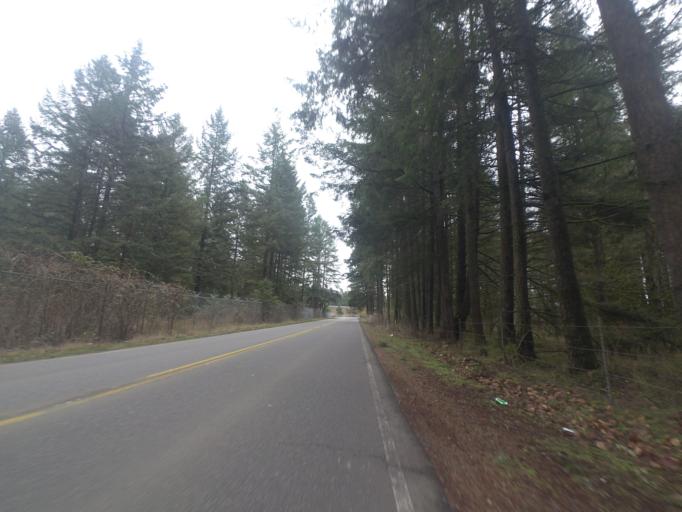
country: US
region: Washington
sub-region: Pierce County
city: McChord Air Force Base
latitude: 47.1179
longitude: -122.5040
